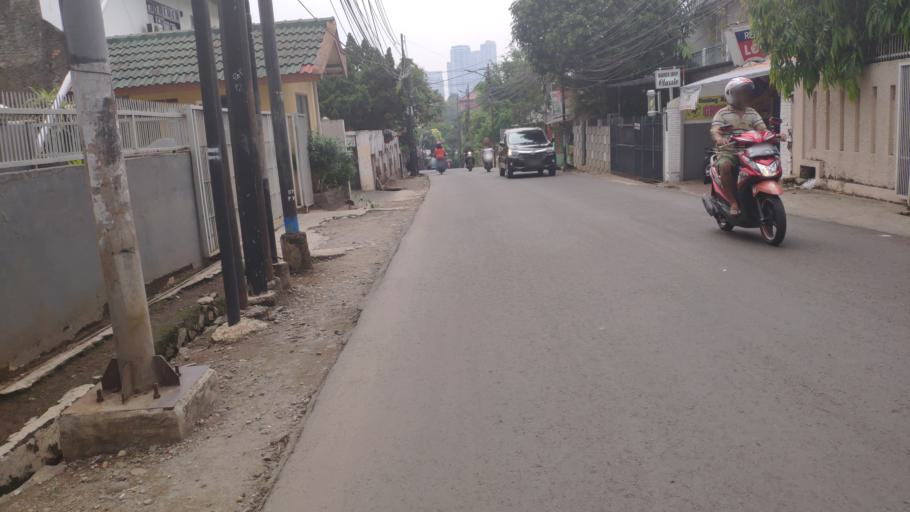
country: ID
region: Jakarta Raya
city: Jakarta
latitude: -6.2593
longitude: 106.8278
